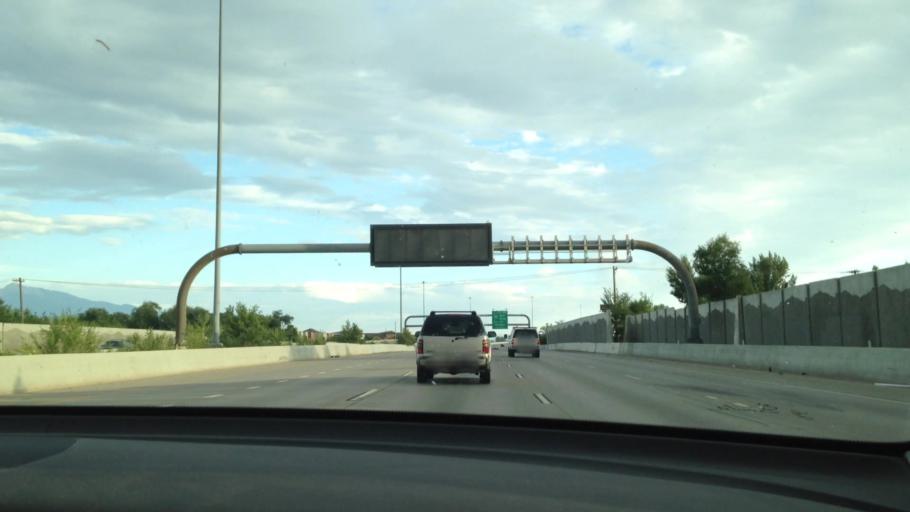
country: US
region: Utah
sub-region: Salt Lake County
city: Salt Lake City
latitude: 40.7772
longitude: -111.9107
